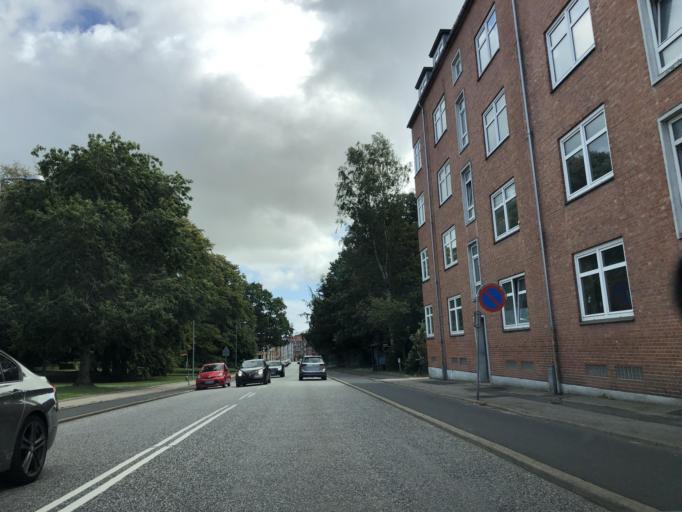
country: DK
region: Central Jutland
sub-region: Randers Kommune
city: Randers
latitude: 56.4664
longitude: 10.0232
